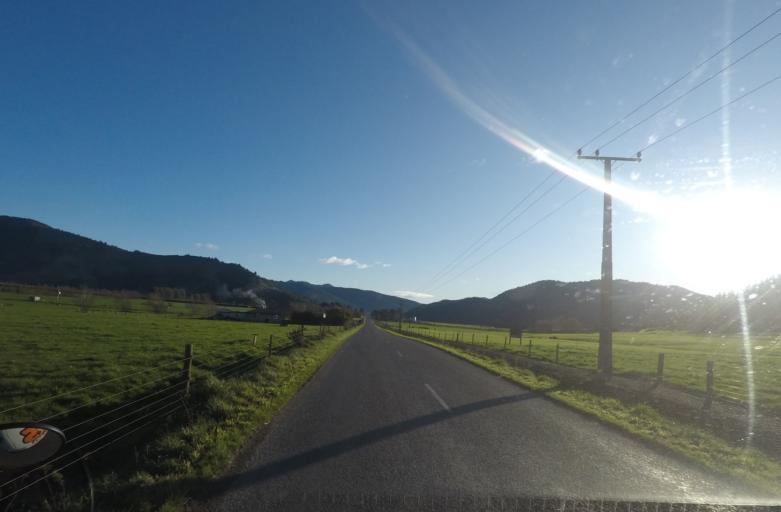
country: NZ
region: Marlborough
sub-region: Marlborough District
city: Picton
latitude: -41.2897
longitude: 173.8753
